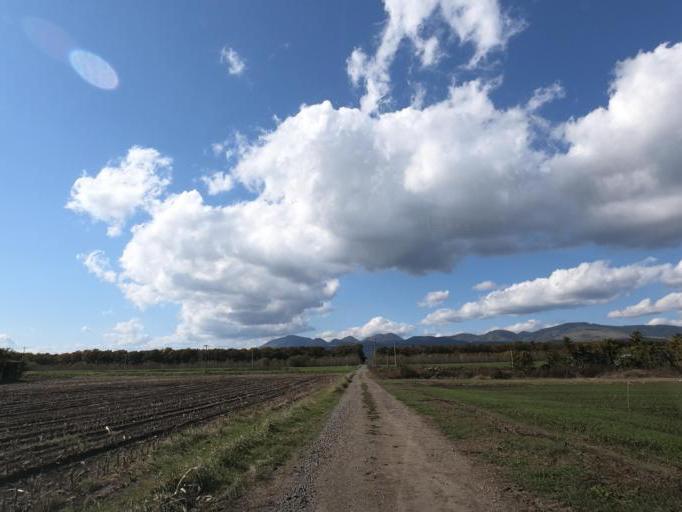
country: JP
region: Hokkaido
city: Otofuke
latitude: 43.2363
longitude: 143.2559
